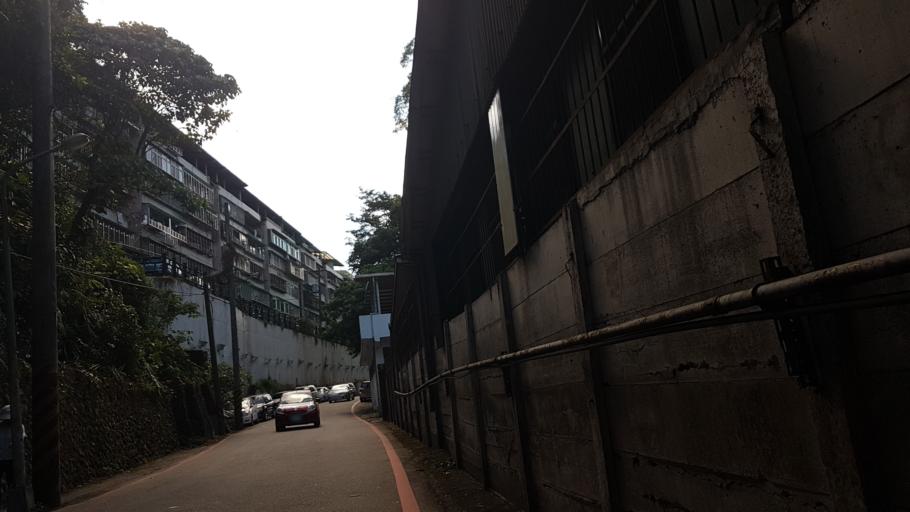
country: TW
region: Taipei
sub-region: Taipei
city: Banqiao
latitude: 24.9508
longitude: 121.5306
